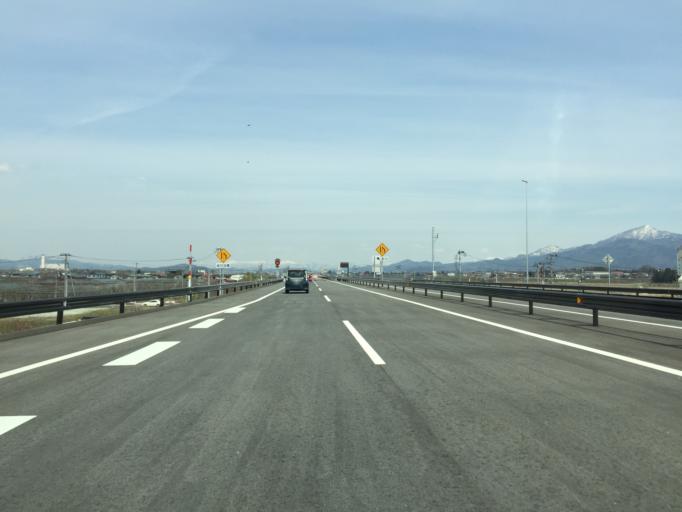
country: JP
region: Yamagata
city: Higashine
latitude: 38.4104
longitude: 140.3474
